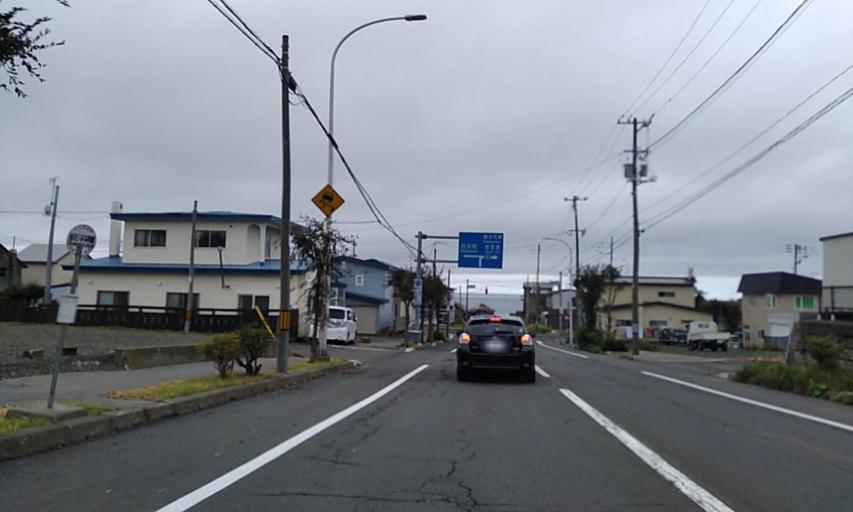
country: JP
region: Hokkaido
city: Nemuro
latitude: 43.3301
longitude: 145.5742
